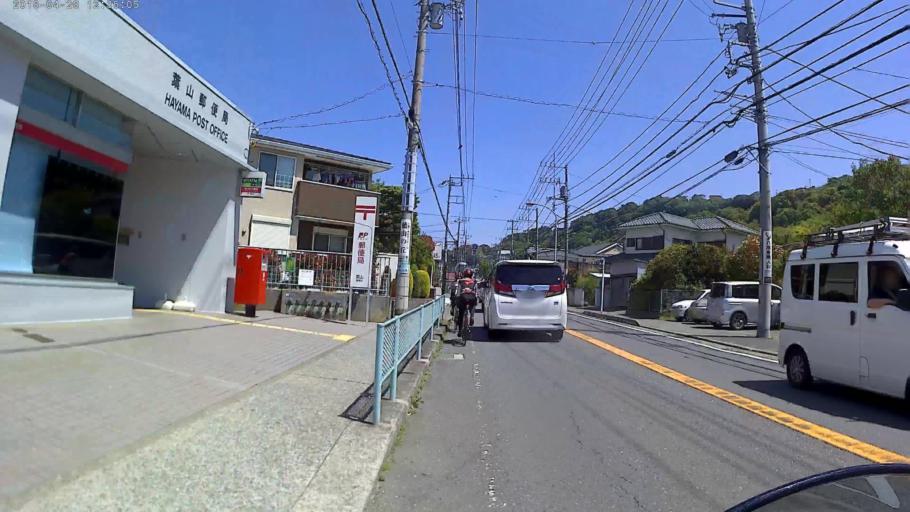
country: JP
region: Kanagawa
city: Hayama
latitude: 35.2654
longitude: 139.5909
